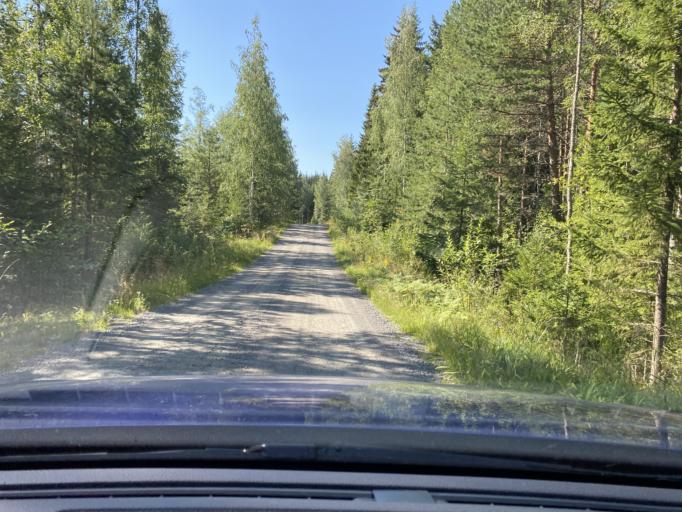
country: FI
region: Central Finland
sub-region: Jaemsae
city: Jaemsae
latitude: 61.8465
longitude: 25.3748
